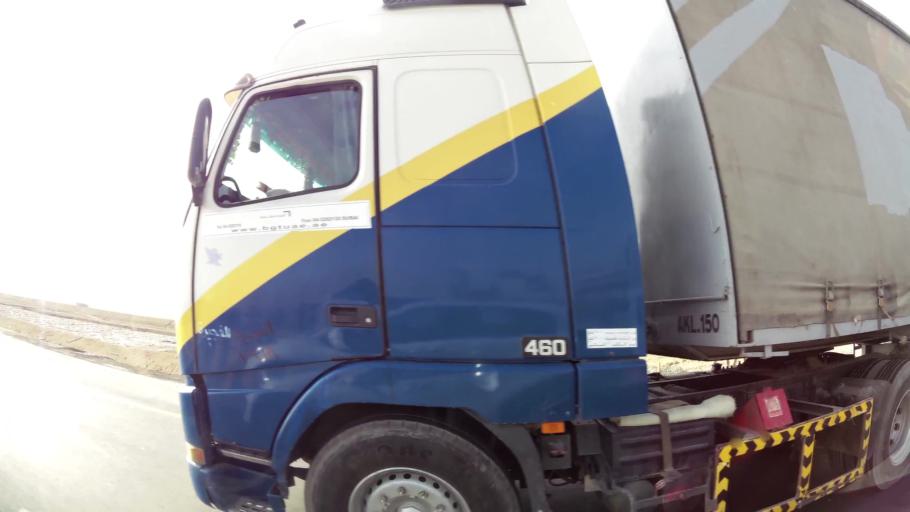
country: AE
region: Abu Dhabi
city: Abu Dhabi
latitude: 24.2426
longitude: 54.4681
